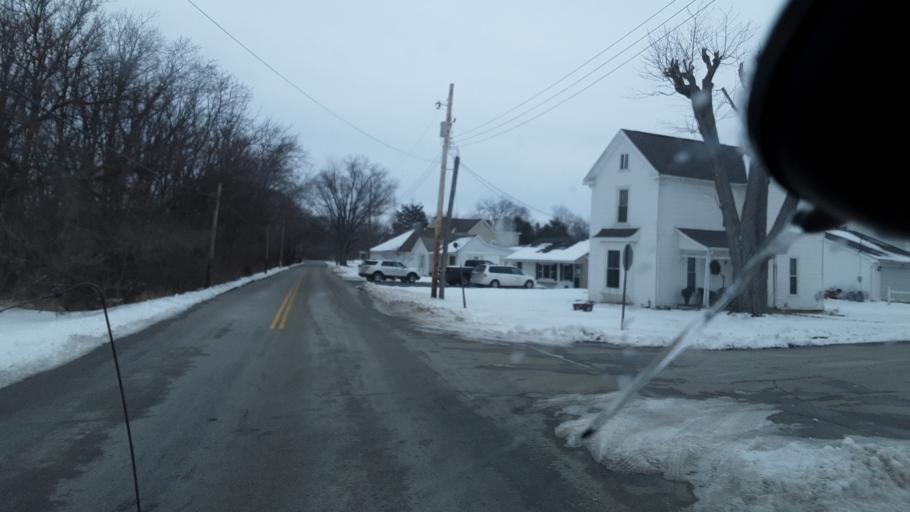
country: US
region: Ohio
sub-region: Madison County
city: Mount Sterling
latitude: 39.7244
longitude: -83.2730
